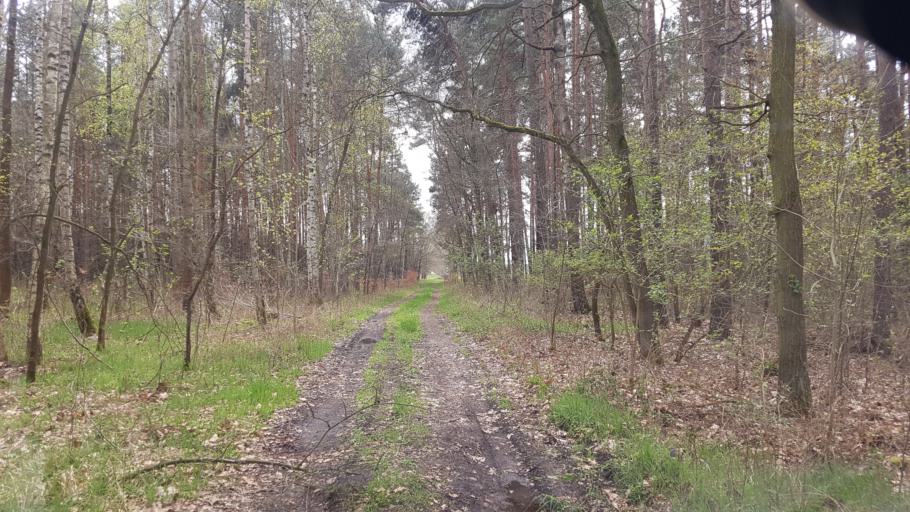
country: DE
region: Brandenburg
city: Bronkow
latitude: 51.6113
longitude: 13.9311
